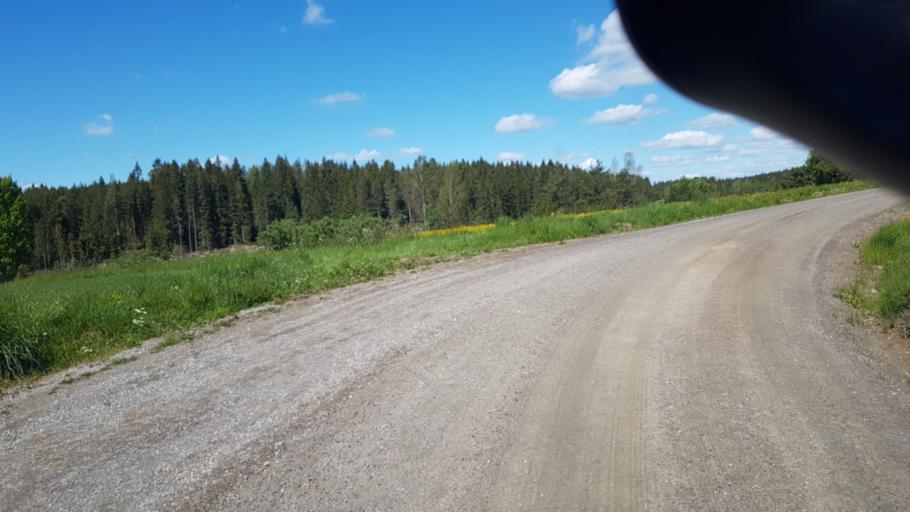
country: SE
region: Vaermland
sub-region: Grums Kommun
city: Grums
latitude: 59.5335
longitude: 12.8853
